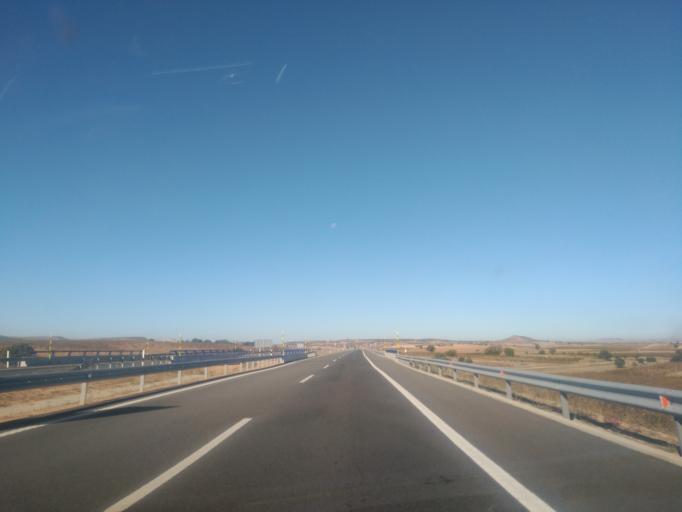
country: ES
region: Castille and Leon
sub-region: Provincia de Burgos
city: Castrillo de la Vega
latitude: 41.6342
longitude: -3.7666
